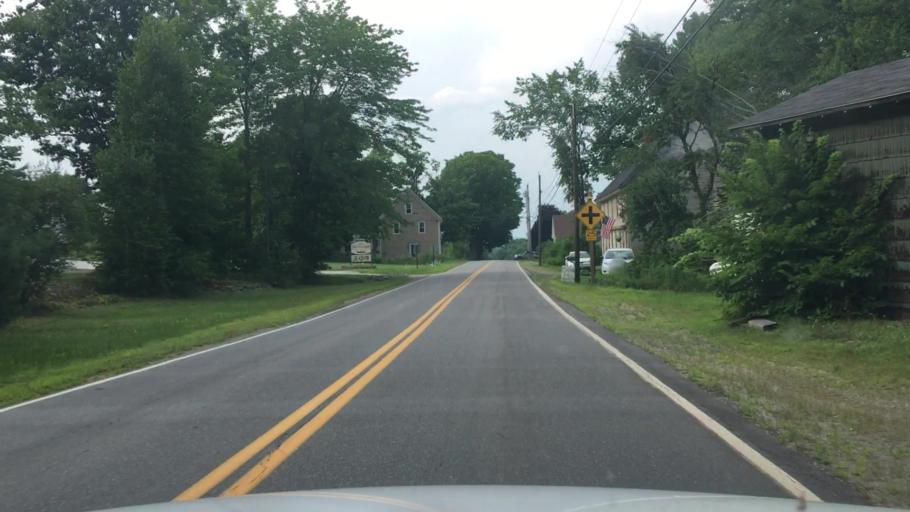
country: US
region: Maine
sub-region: Lincoln County
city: Jefferson
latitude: 44.1827
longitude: -69.3754
